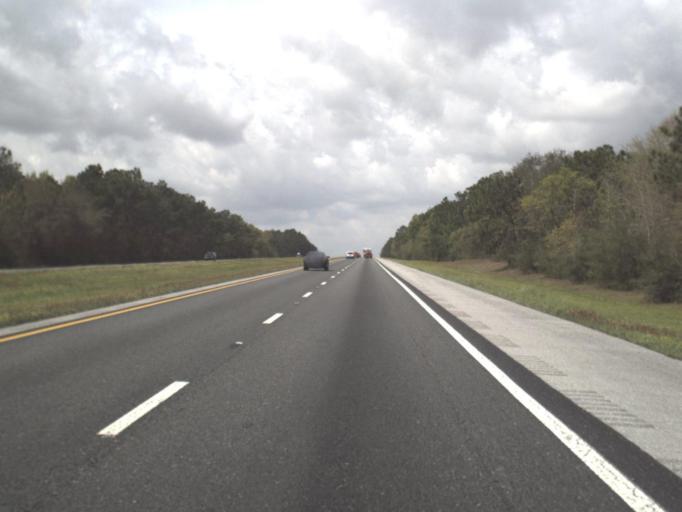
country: US
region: Florida
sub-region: Okaloosa County
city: Crestview
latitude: 30.7154
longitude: -86.6803
